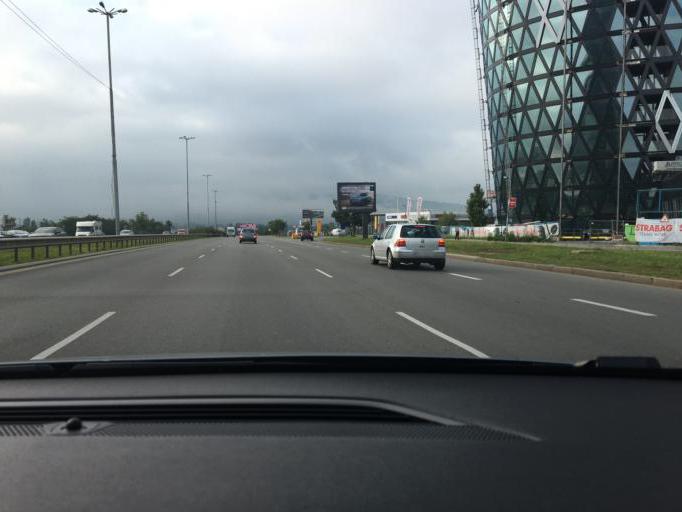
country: BG
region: Sofia-Capital
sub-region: Stolichna Obshtina
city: Sofia
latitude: 42.6465
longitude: 23.3970
